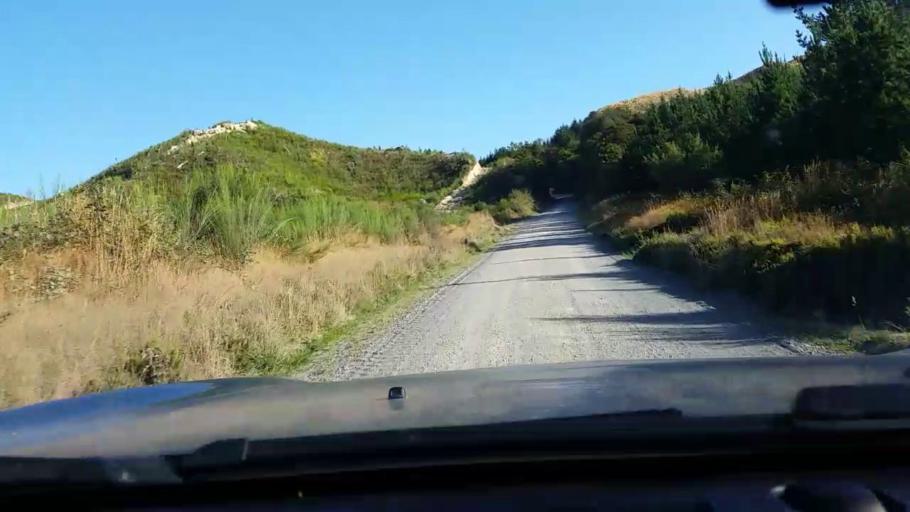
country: NZ
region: Waikato
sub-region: Taupo District
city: Taupo
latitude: -38.4608
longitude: 176.1592
